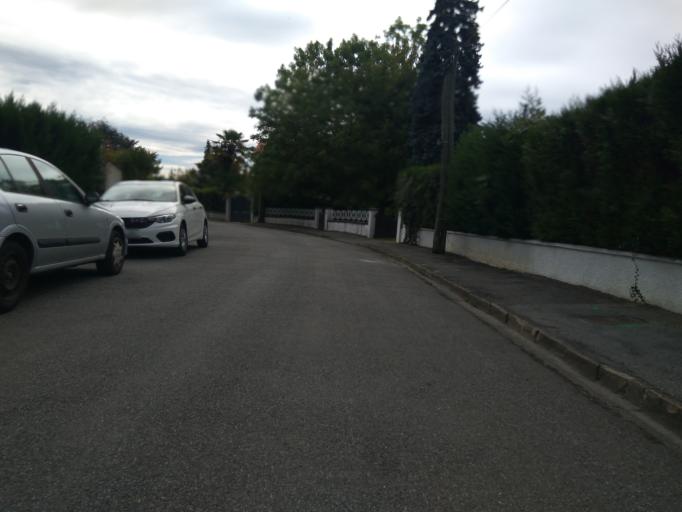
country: FR
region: Aquitaine
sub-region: Departement des Pyrenees-Atlantiques
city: Bizanos
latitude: 43.2981
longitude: -0.3486
